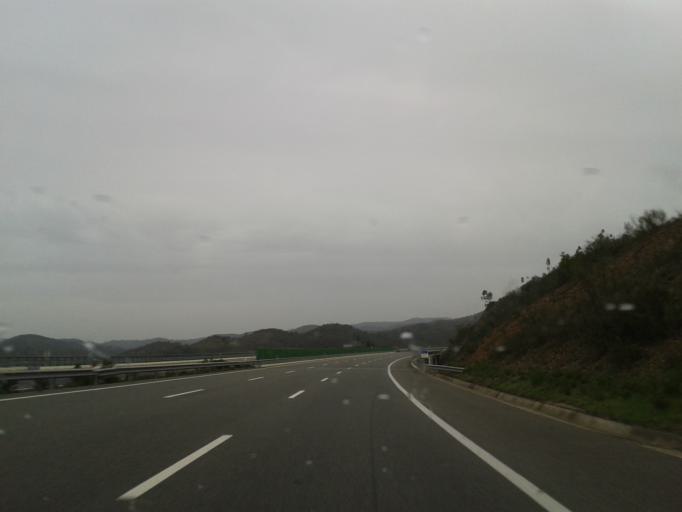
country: PT
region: Faro
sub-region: Silves
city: Sao Bartolomeu de Messines
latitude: 37.3803
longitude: -8.2619
